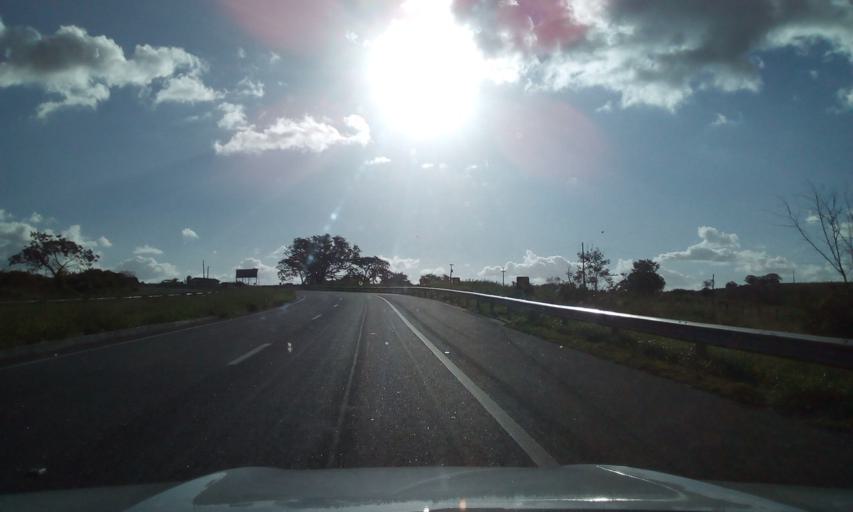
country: BR
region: Paraiba
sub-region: Pilar
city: Pilar
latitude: -7.1850
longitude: -35.1956
